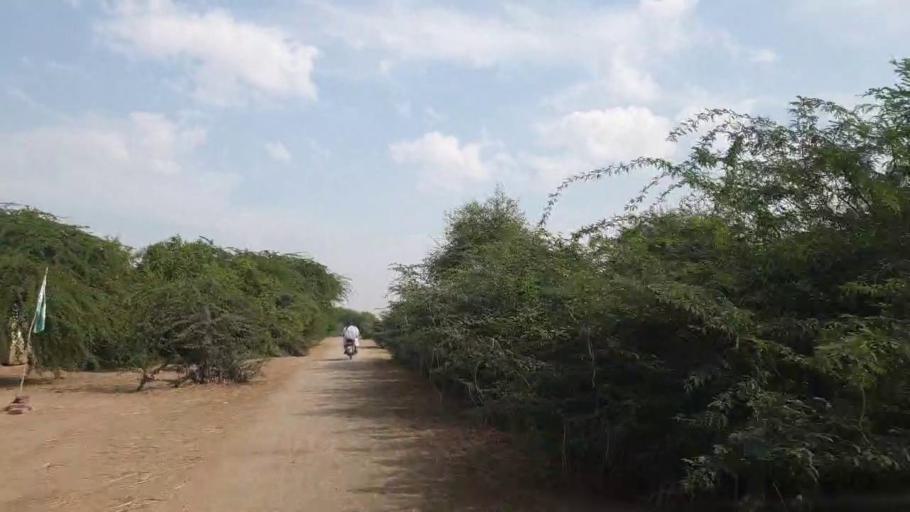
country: PK
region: Sindh
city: Rajo Khanani
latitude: 24.9370
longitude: 68.9920
